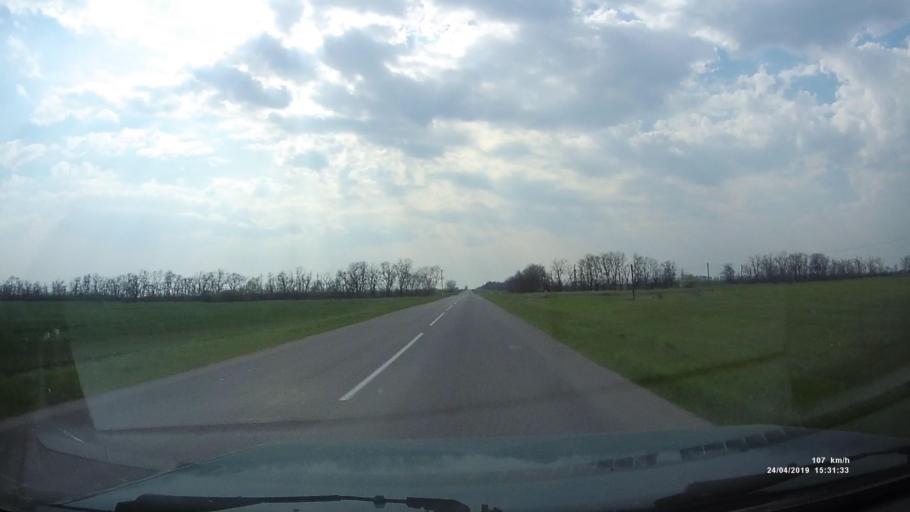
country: RU
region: Rostov
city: Remontnoye
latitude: 46.6002
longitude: 42.9814
